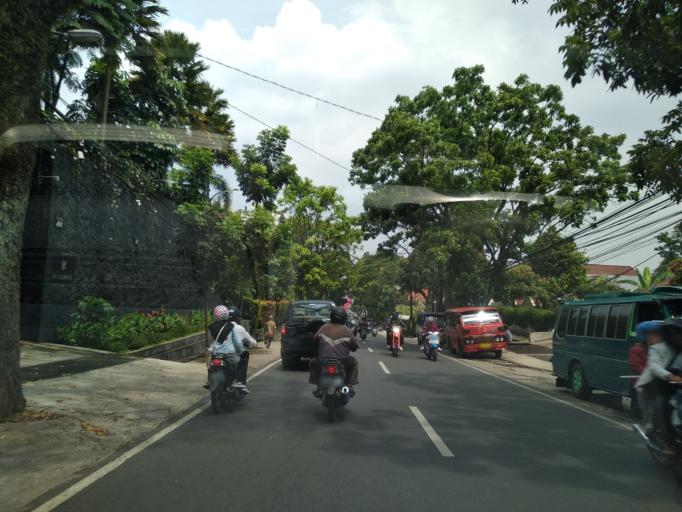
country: ID
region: West Java
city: Lembang
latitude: -6.8572
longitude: 107.5953
